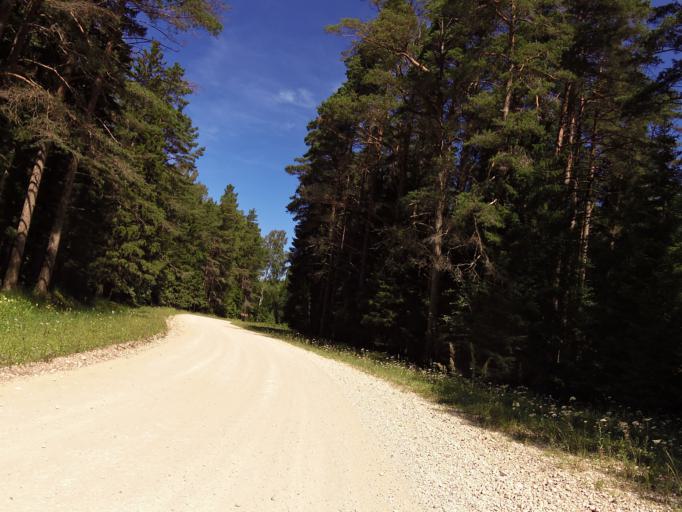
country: EE
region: Hiiumaa
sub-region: Kaerdla linn
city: Kardla
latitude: 58.9193
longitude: 22.3508
